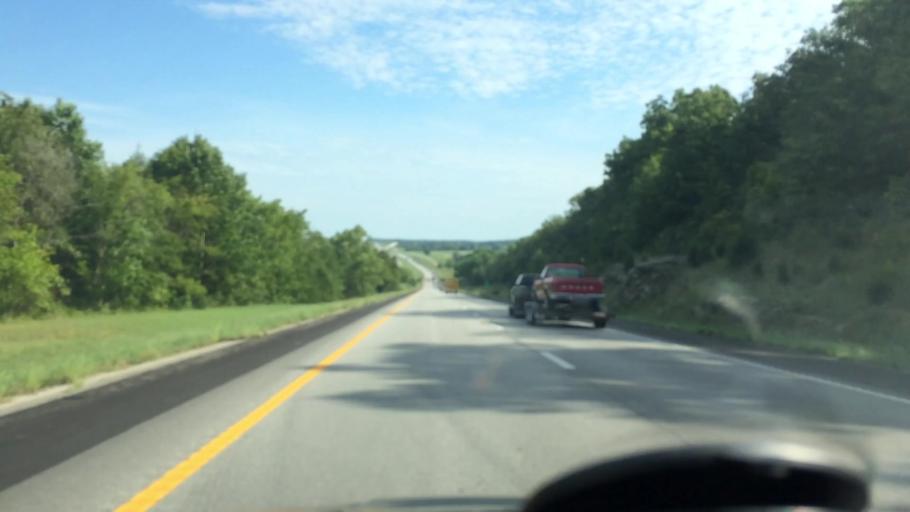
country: US
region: Missouri
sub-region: Webster County
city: Marshfield
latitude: 37.4040
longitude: -92.8938
